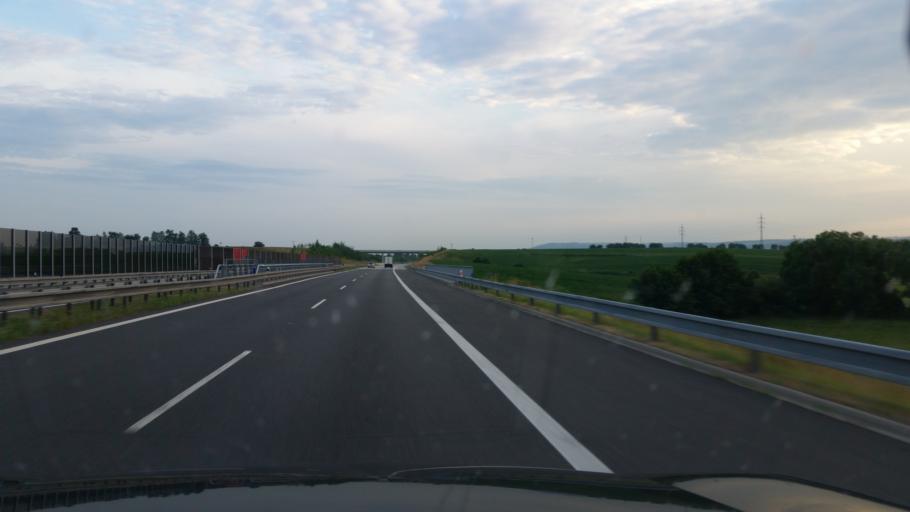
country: CZ
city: Bilovec
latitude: 49.7092
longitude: 17.9957
